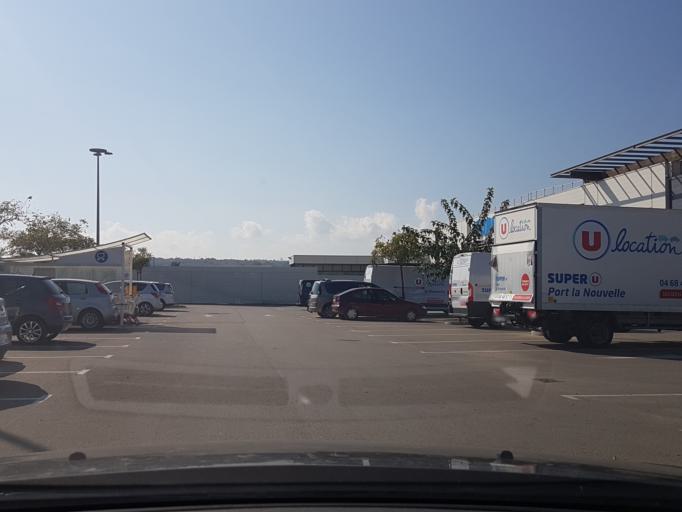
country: FR
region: Languedoc-Roussillon
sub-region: Departement de l'Aude
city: Port-la-Nouvelle
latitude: 43.0151
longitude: 3.0497
